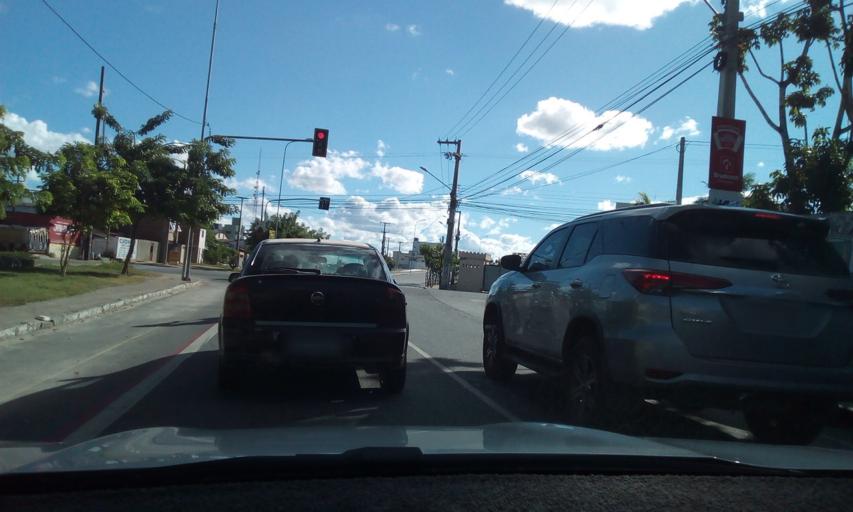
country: BR
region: Paraiba
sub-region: Campina Grande
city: Campina Grande
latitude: -7.2293
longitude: -35.8932
